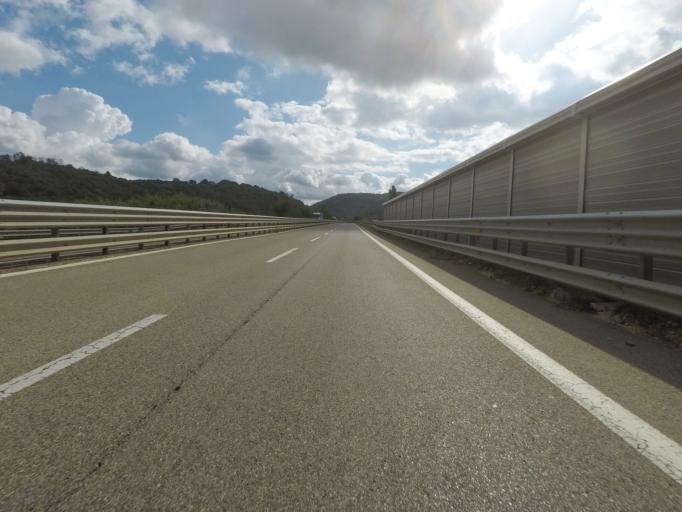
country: IT
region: Tuscany
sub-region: Provincia di Siena
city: Rapolano Terme
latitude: 43.2953
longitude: 11.6049
